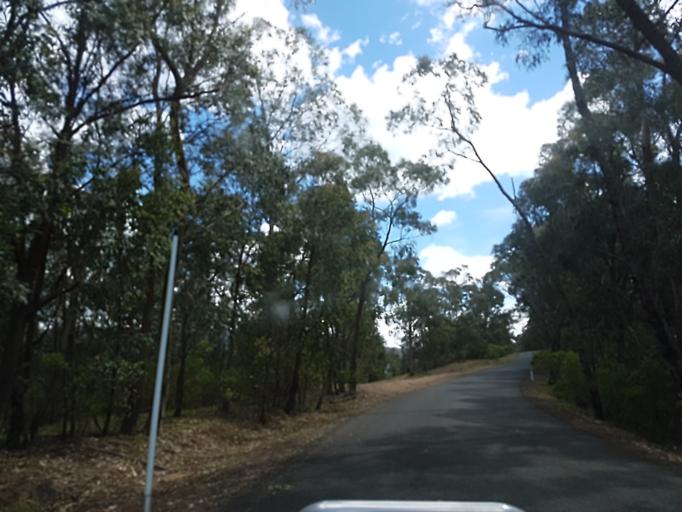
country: AU
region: Victoria
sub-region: East Gippsland
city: Bairnsdale
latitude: -37.4146
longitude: 147.2512
